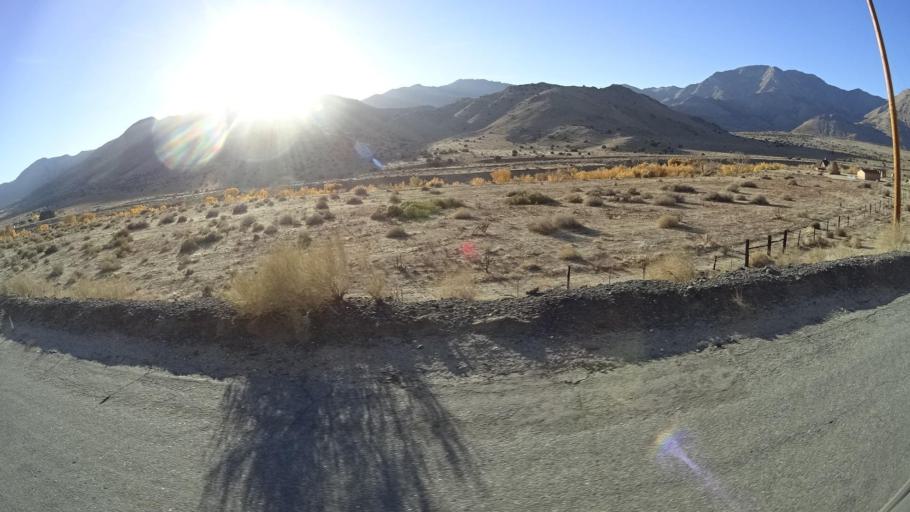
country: US
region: California
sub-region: Kern County
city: Weldon
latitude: 35.5675
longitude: -118.2468
